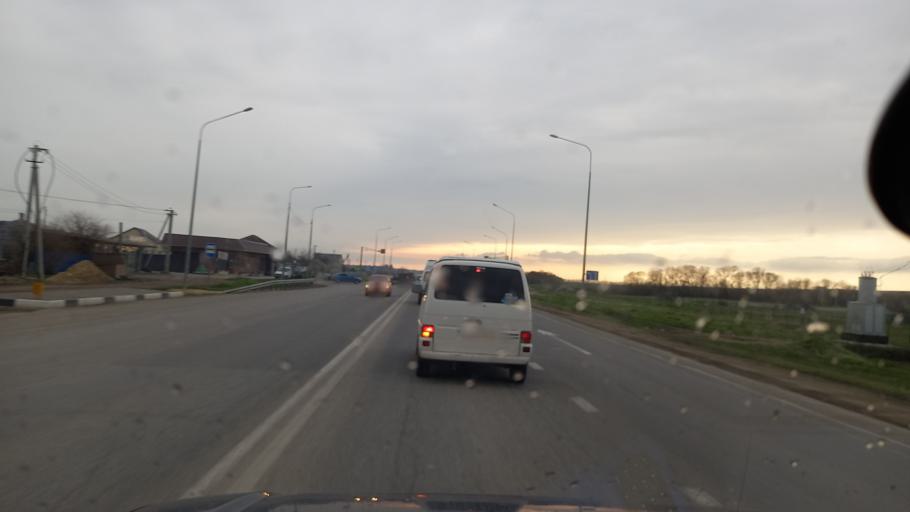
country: RU
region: Krasnodarskiy
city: Anapskaya
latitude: 44.8968
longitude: 37.4603
